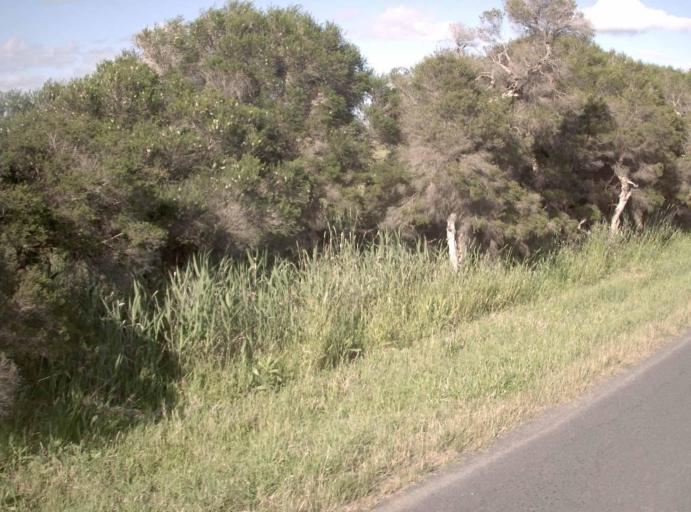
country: AU
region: Victoria
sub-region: Bass Coast
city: North Wonthaggi
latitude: -38.6081
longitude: 145.6127
